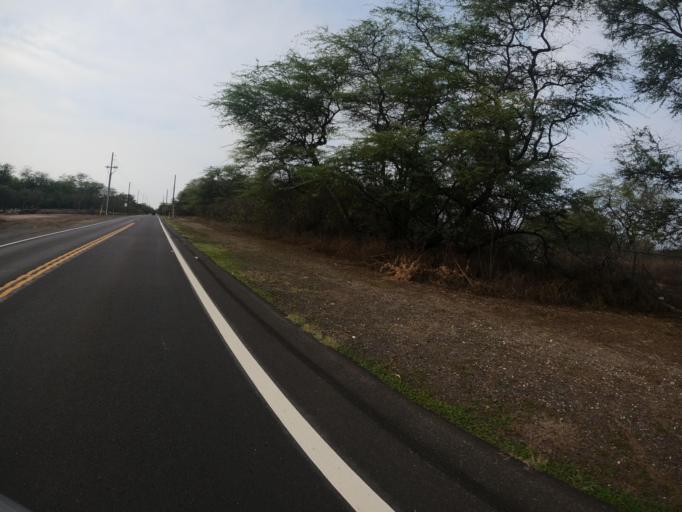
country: US
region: Hawaii
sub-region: Honolulu County
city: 'Ewa Villages
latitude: 21.3130
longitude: -158.0558
